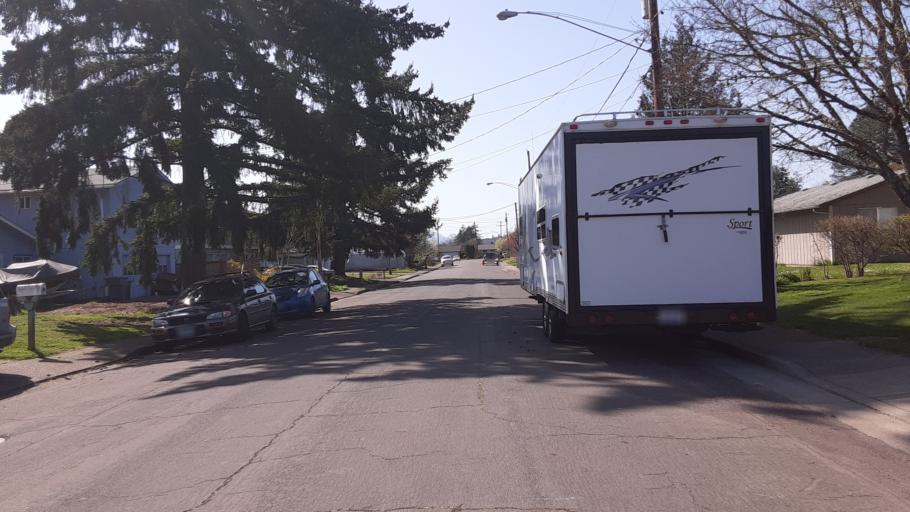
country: US
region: Oregon
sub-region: Benton County
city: Corvallis
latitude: 44.5397
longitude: -123.2577
